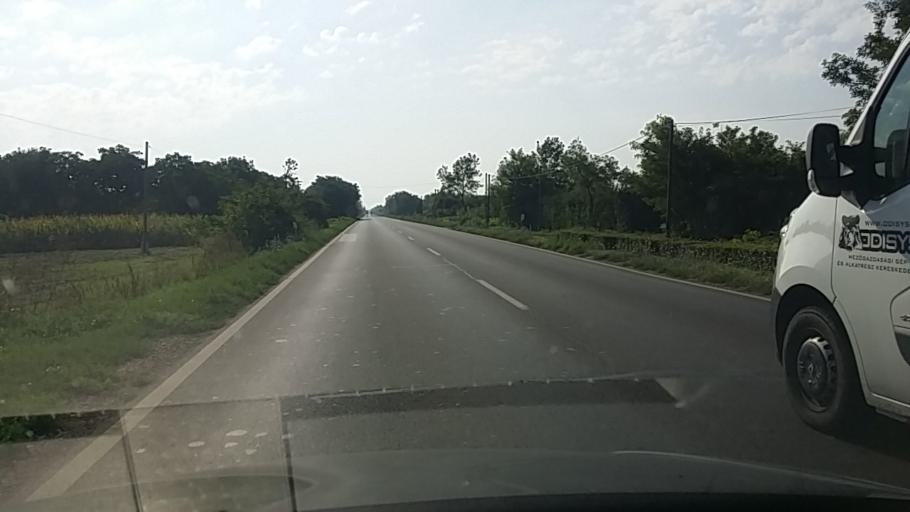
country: HU
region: Bekes
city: Kondoros
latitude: 46.8055
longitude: 20.7023
